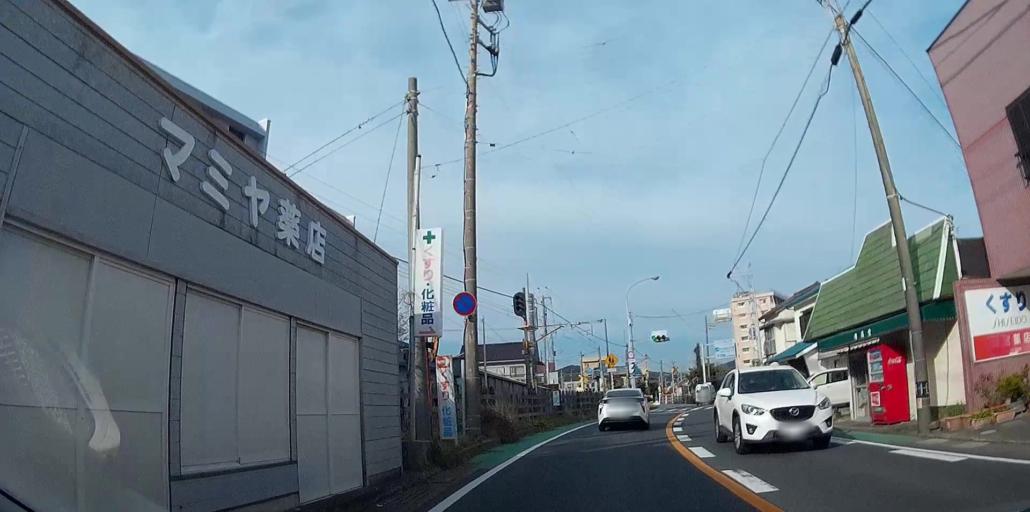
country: JP
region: Chiba
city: Kawaguchi
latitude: 35.0394
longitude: 140.0183
